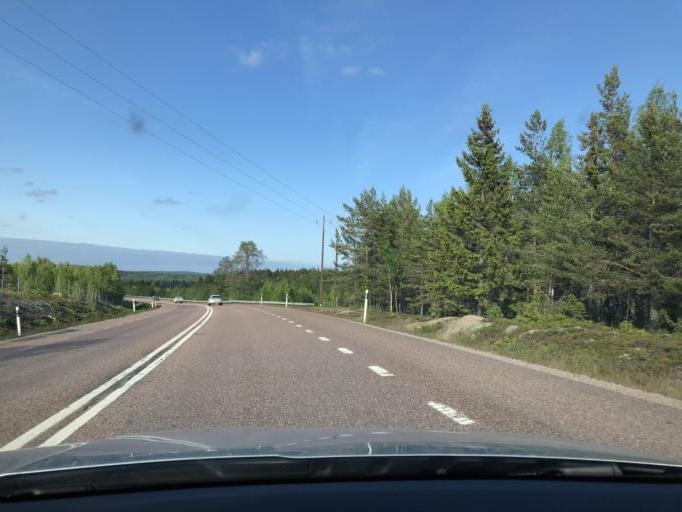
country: SE
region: Gaevleborg
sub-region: Nordanstigs Kommun
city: Bergsjoe
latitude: 61.9155
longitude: 17.2063
